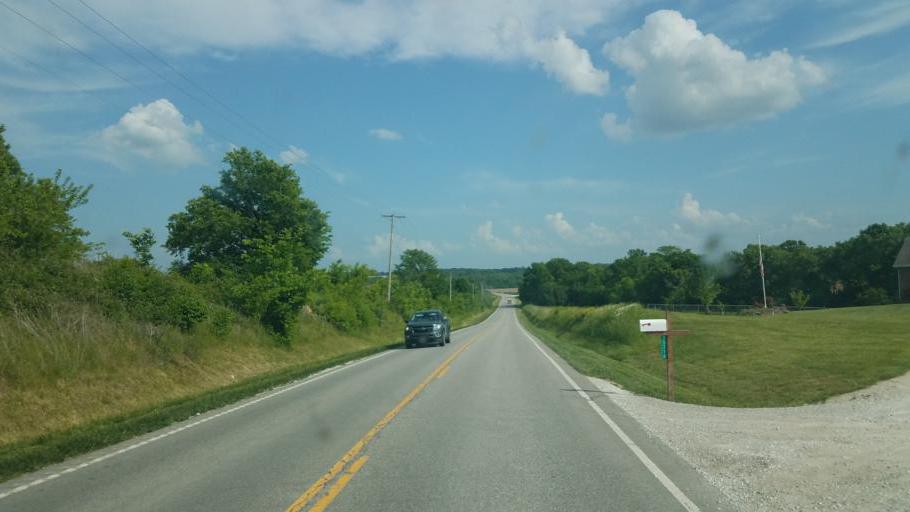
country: US
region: Missouri
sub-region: Cooper County
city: Boonville
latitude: 38.9074
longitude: -92.6777
